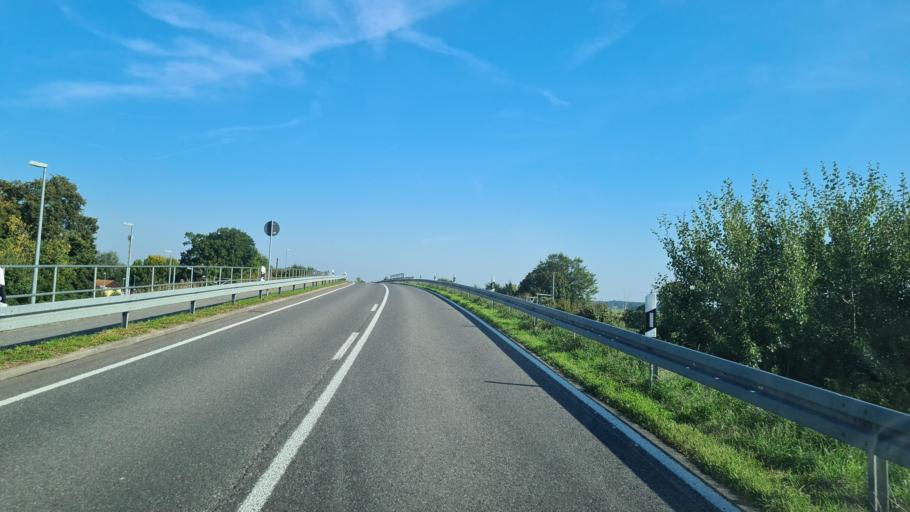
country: DE
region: Brandenburg
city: Friesack
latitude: 52.7585
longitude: 12.5883
